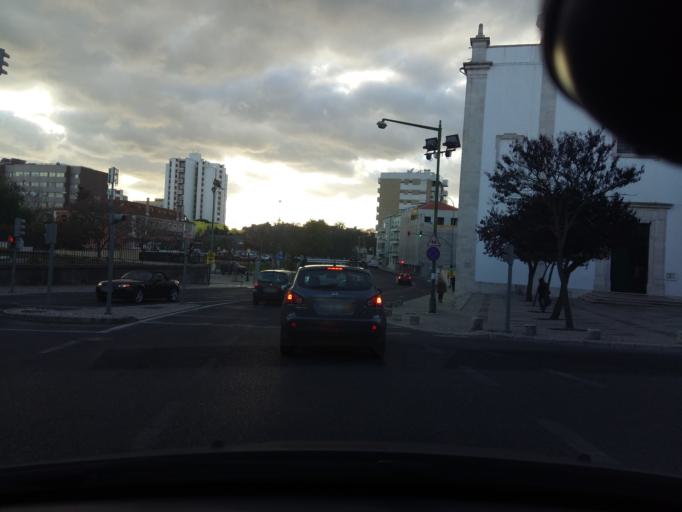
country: PT
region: Lisbon
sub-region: Odivelas
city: Pontinha
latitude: 38.7604
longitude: -9.1842
